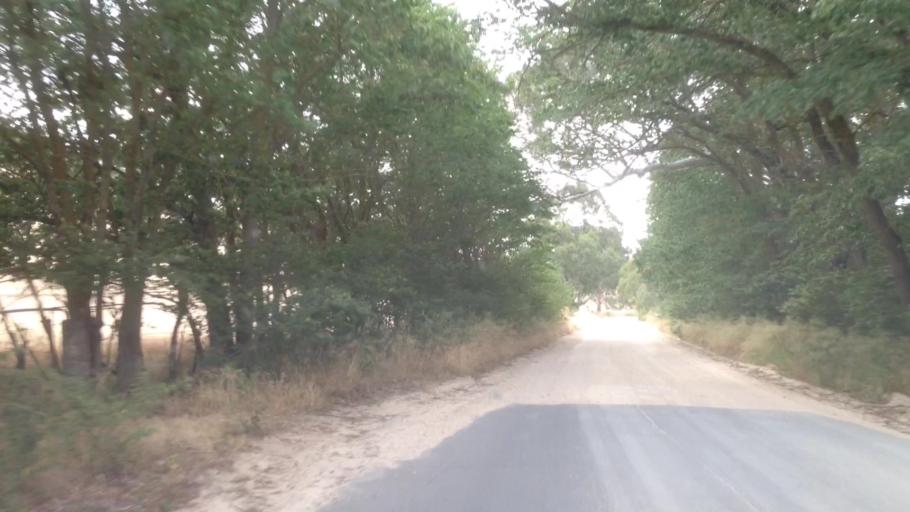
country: AU
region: South Australia
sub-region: Barossa
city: Lyndoch
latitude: -34.6064
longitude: 138.9500
